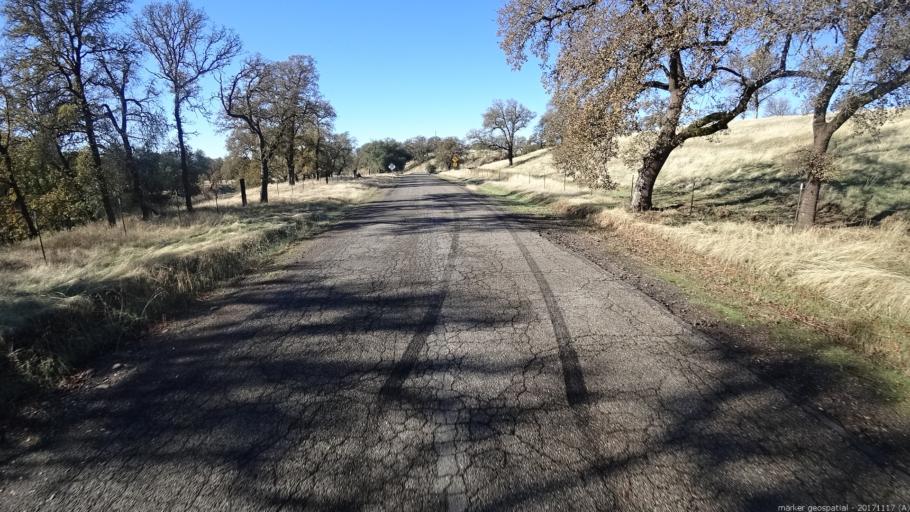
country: US
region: California
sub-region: Shasta County
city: Cottonwood
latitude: 40.4226
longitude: -122.1892
